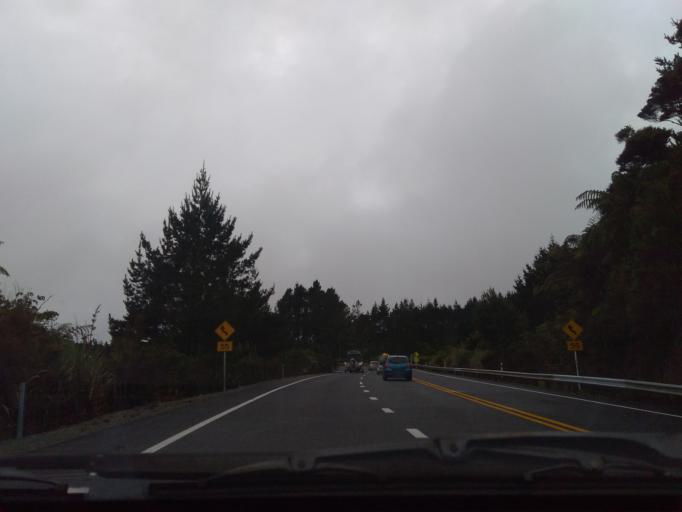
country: NZ
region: Northland
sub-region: Whangarei
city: Ruakaka
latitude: -36.0707
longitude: 174.4201
